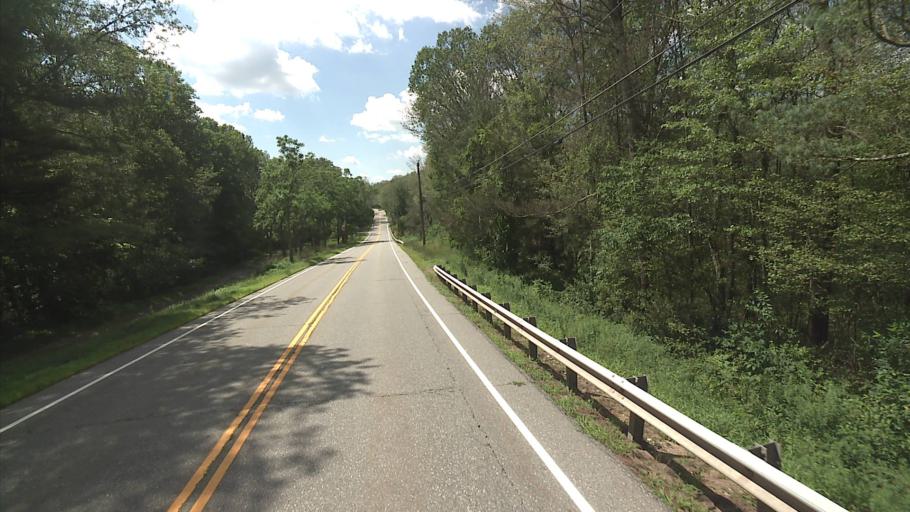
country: US
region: Connecticut
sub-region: Windham County
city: Windham
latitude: 41.8259
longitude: -72.1012
